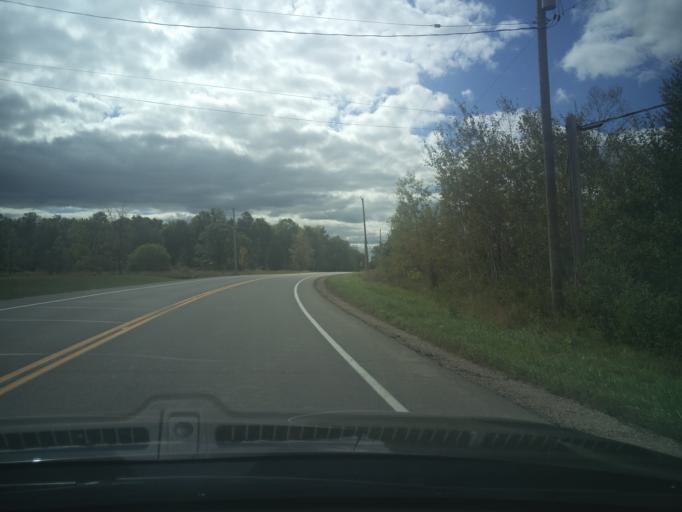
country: CA
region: Ontario
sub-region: Lanark County
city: Smiths Falls
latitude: 45.0089
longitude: -76.0813
